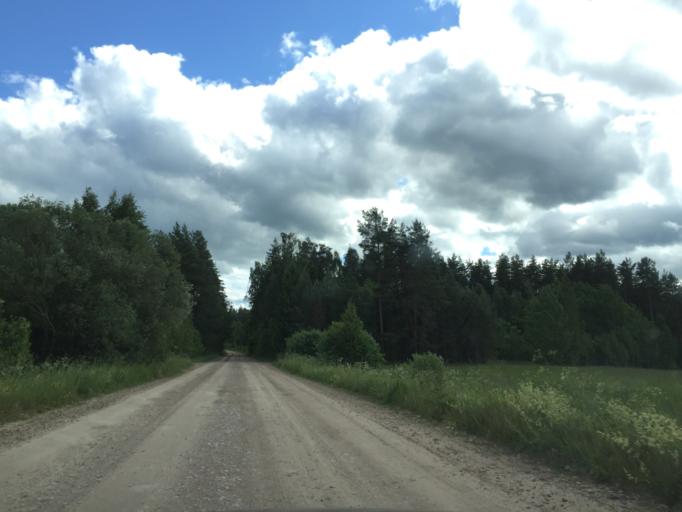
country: LV
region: Vecumnieki
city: Vecumnieki
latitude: 56.4964
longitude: 24.4078
